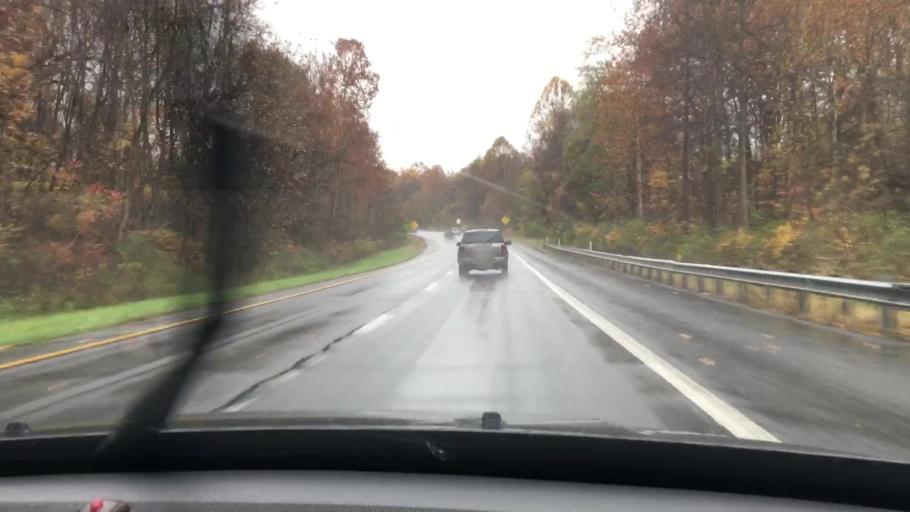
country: US
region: Pennsylvania
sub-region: Lancaster County
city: Willow Street
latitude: 39.9237
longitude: -76.2531
